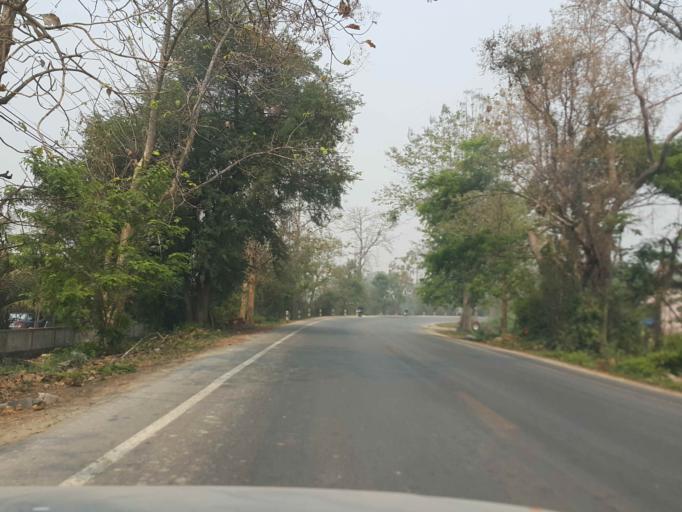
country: TH
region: Chiang Mai
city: Mae Taeng
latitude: 19.0013
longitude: 98.9733
